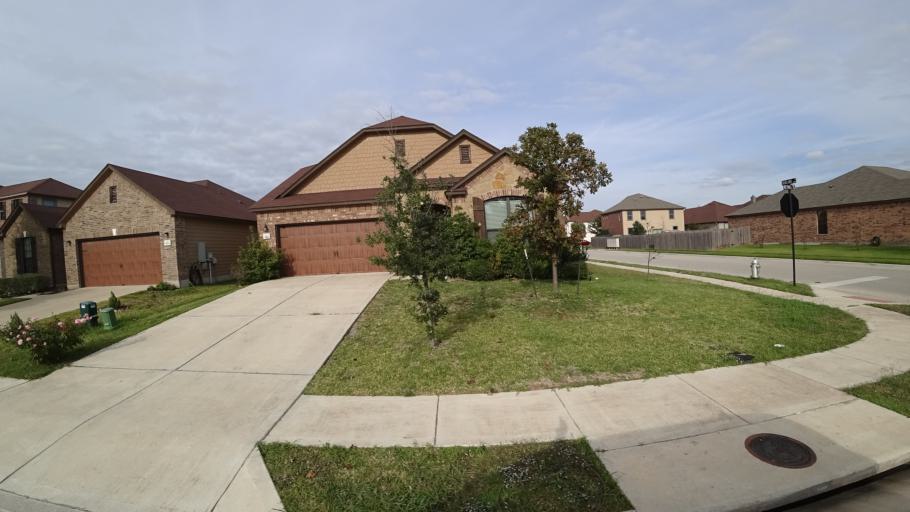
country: US
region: Texas
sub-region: Travis County
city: Wells Branch
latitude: 30.4301
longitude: -97.6607
